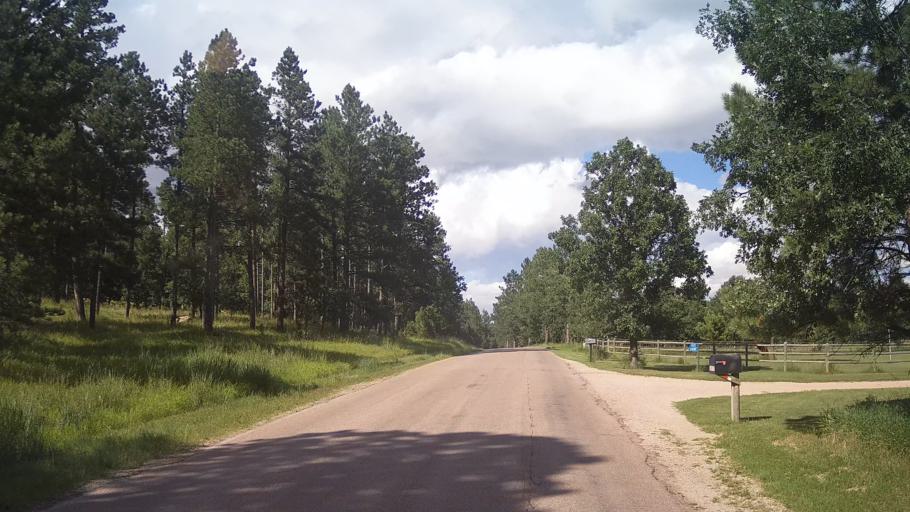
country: US
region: South Dakota
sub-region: Pennington County
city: Colonial Pine Hills
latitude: 43.8443
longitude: -103.3846
